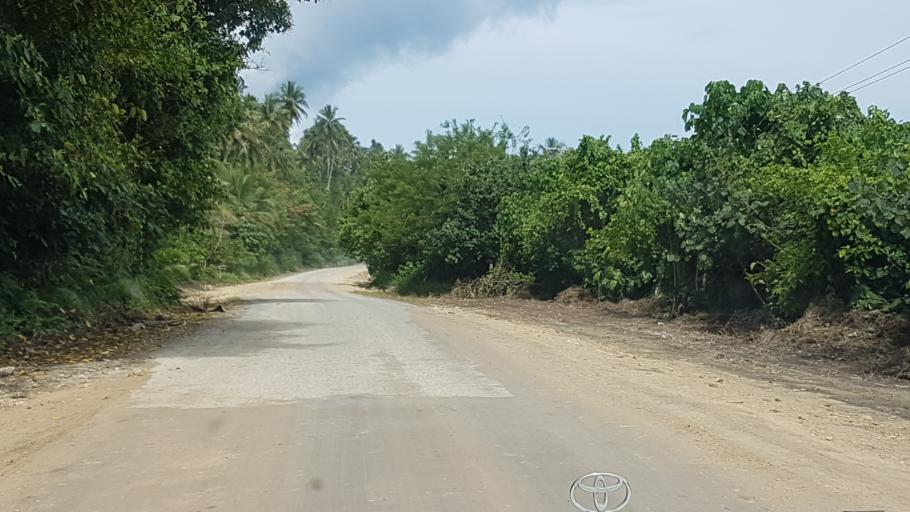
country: PG
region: Madang
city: Madang
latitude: -4.8467
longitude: 145.8025
